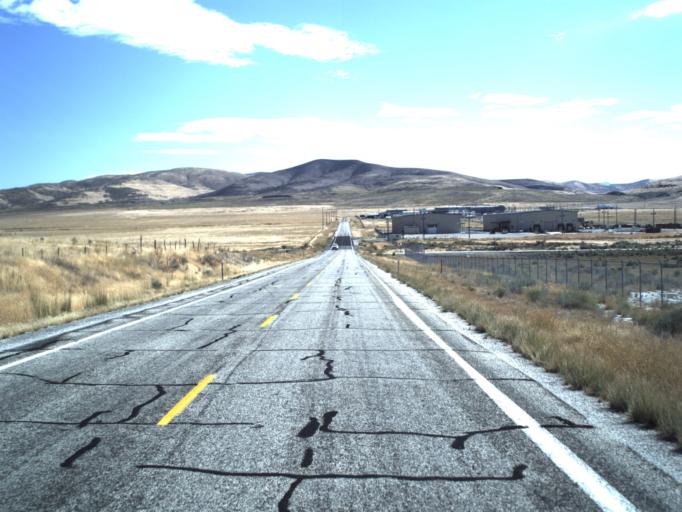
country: US
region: Utah
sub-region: Box Elder County
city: Tremonton
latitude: 41.7223
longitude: -112.4466
